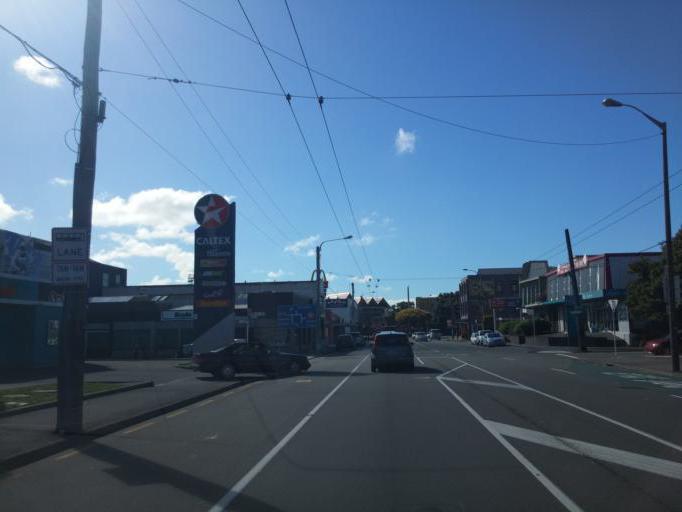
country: NZ
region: Wellington
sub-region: Wellington City
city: Wellington
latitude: -41.3026
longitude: 174.7793
